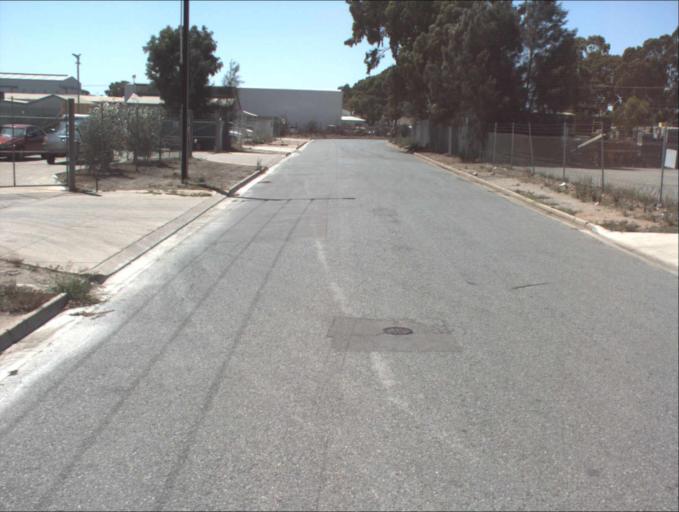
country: AU
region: South Australia
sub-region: Charles Sturt
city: Woodville North
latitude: -34.8475
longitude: 138.5531
